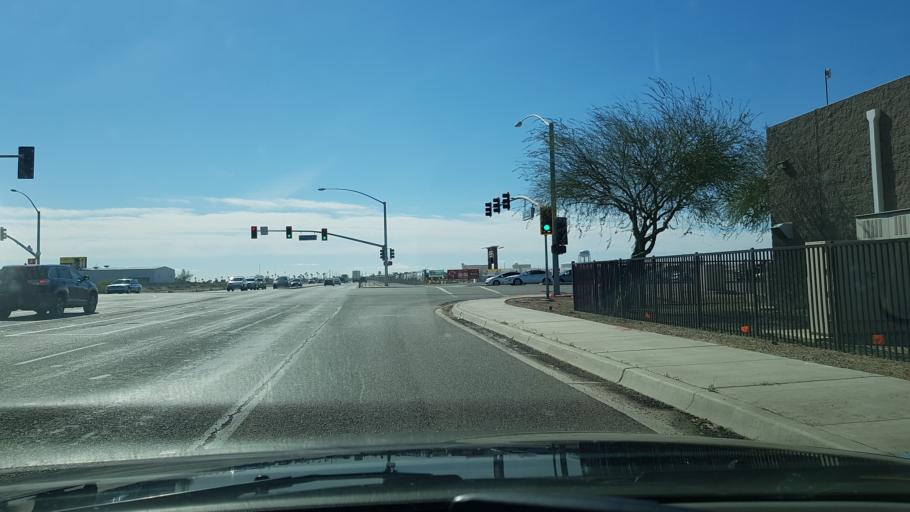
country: US
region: Arizona
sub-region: Yuma County
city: Yuma
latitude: 32.6702
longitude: -114.5817
